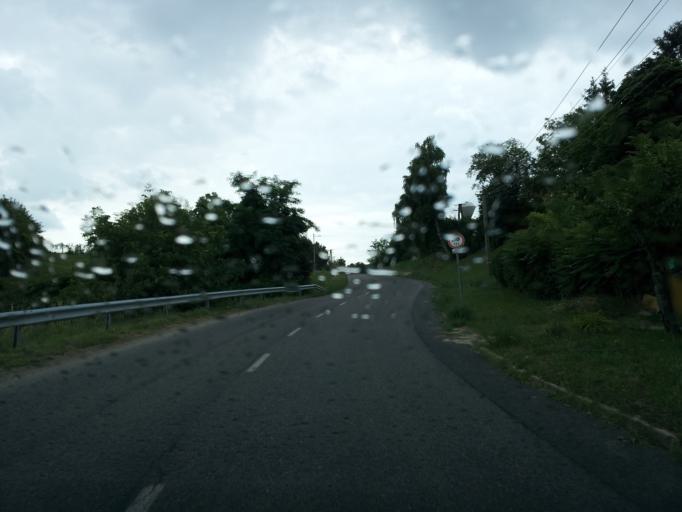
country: HU
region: Zala
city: Turje
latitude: 47.0857
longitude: 17.0240
